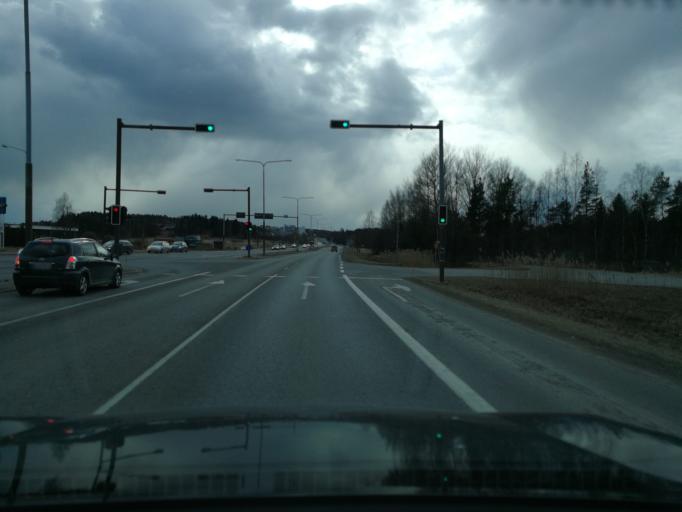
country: FI
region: Varsinais-Suomi
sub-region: Turku
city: Kaarina
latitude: 60.4673
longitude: 22.3485
